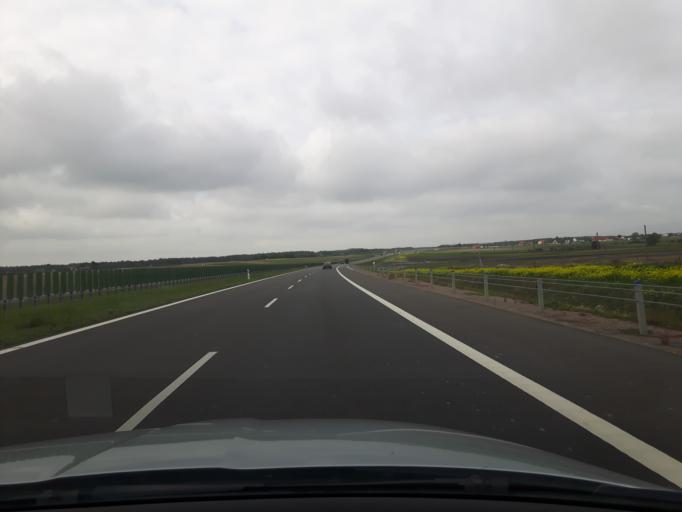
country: PL
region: Swietokrzyskie
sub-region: Powiat jedrzejowski
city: Sobkow
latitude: 50.6962
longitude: 20.3900
